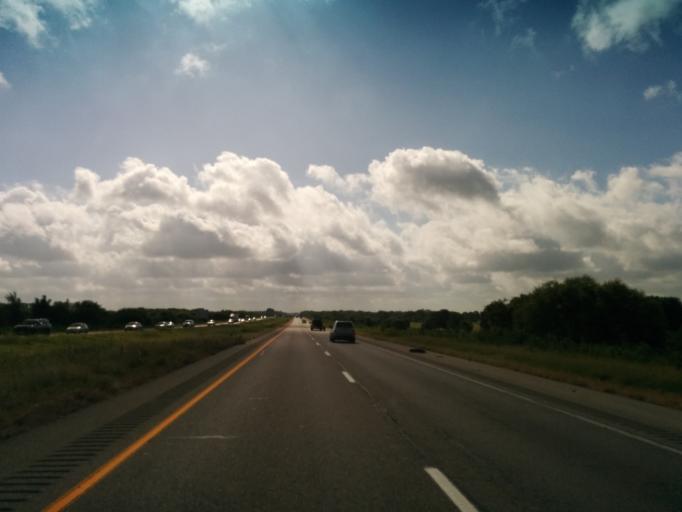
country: US
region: Texas
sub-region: Caldwell County
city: Luling
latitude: 29.6503
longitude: -97.6495
